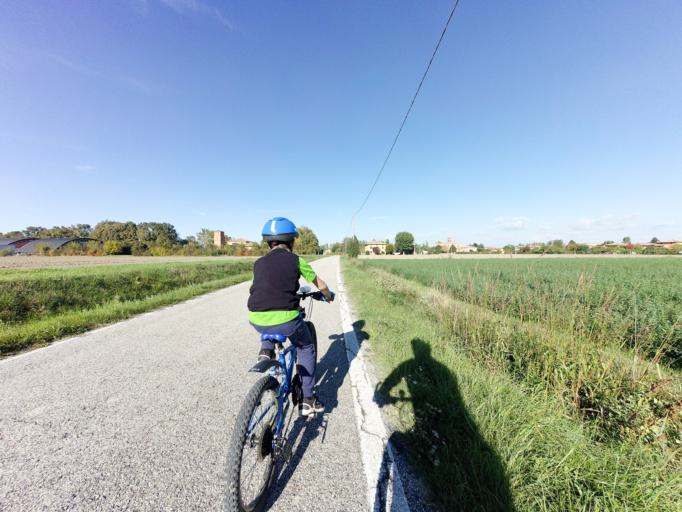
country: IT
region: Emilia-Romagna
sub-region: Provincia di Bologna
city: Bentivoglio
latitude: 44.6010
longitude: 11.4169
